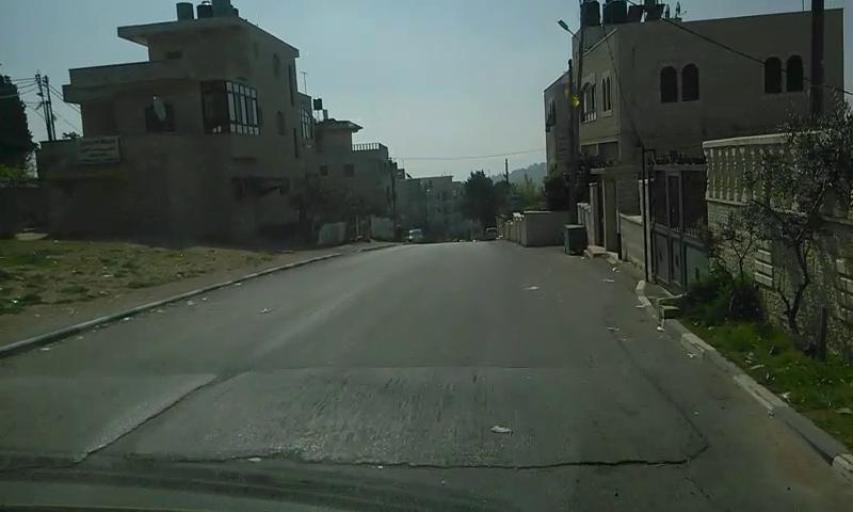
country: PS
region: West Bank
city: Dayr Jarir
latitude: 31.9653
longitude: 35.2931
